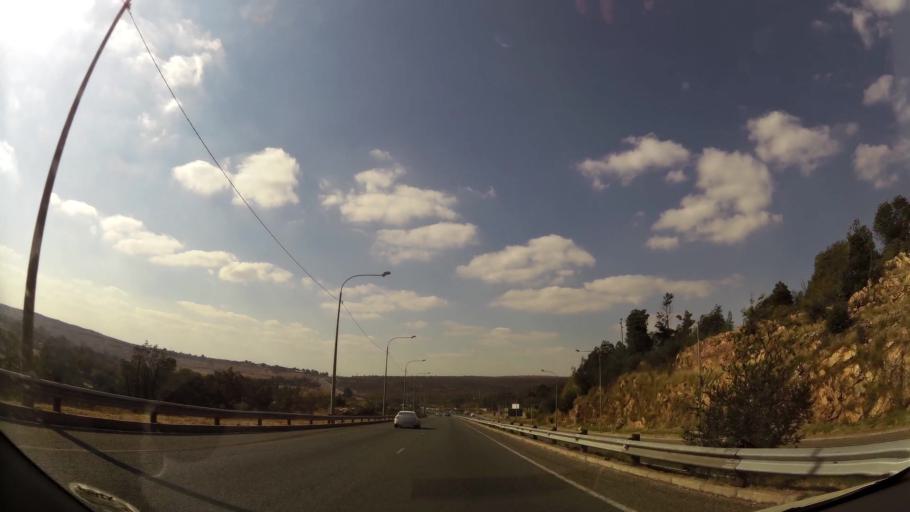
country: ZA
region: Gauteng
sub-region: West Rand District Municipality
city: Krugersdorp
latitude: -26.0749
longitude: 27.7980
